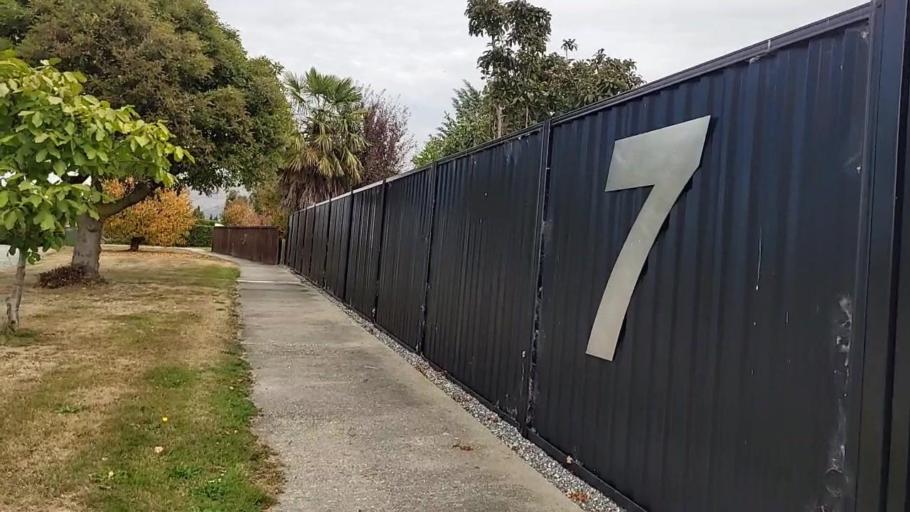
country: NZ
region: Otago
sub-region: Queenstown-Lakes District
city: Kingston
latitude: -45.4792
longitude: 169.3127
